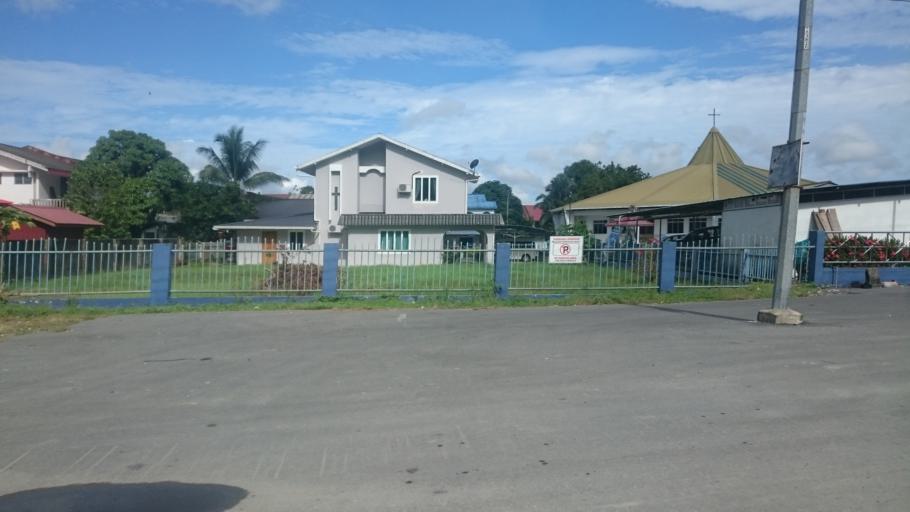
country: MY
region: Sarawak
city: Limbang
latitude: 4.7398
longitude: 115.0020
